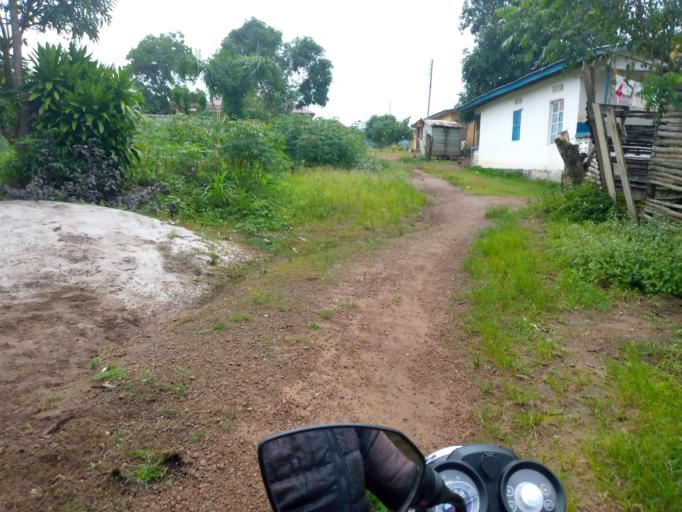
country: SL
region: Eastern Province
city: Kenema
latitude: 7.8437
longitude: -11.2016
